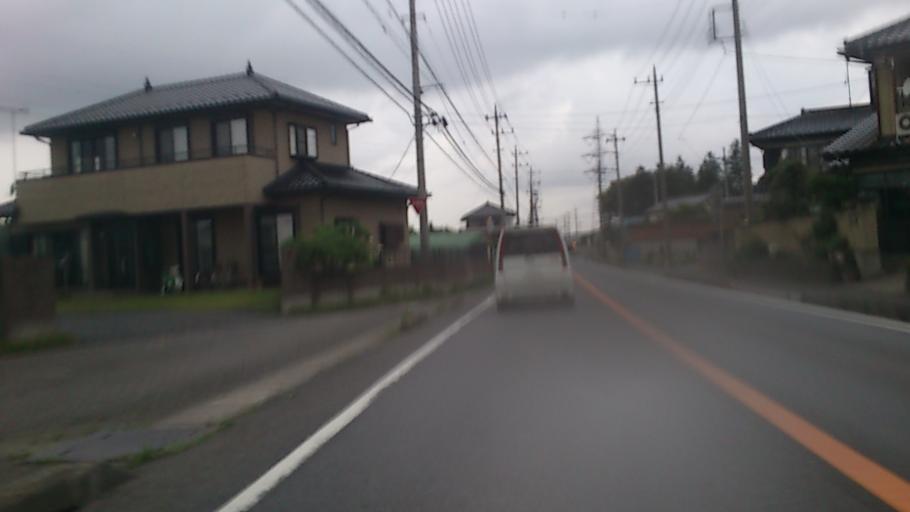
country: JP
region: Ibaraki
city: Sakai
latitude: 36.1404
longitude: 139.7614
